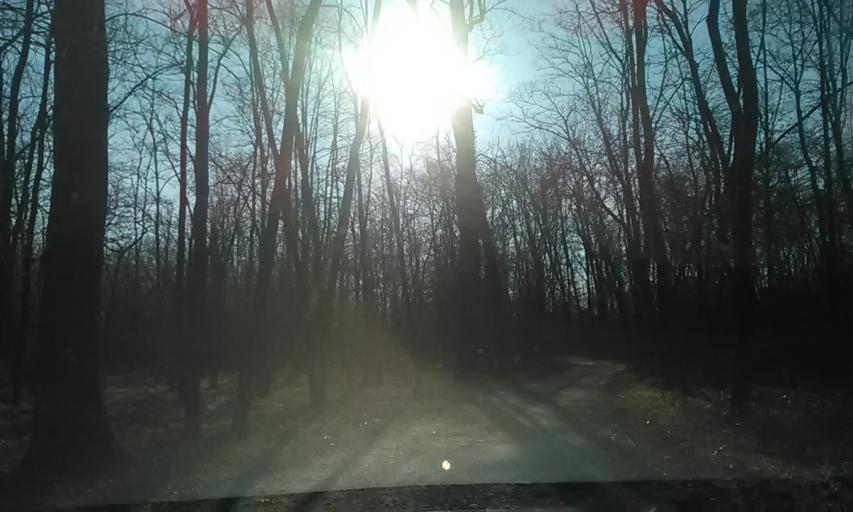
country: IT
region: Piedmont
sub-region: Provincia di Vercelli
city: Lenta
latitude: 45.5827
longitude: 8.3829
